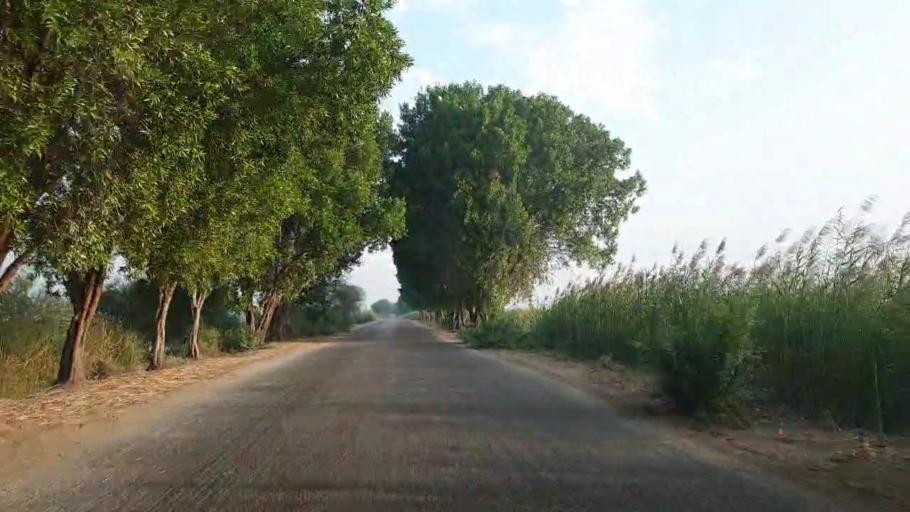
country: PK
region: Sindh
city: Tando Bago
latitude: 24.7297
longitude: 68.9438
